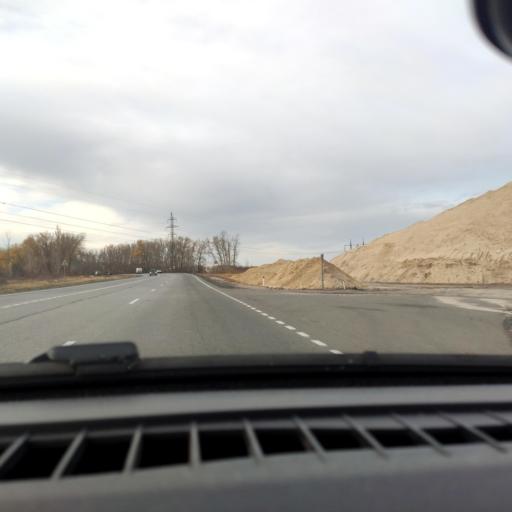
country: RU
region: Voronezj
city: Ostrogozhsk
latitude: 50.9441
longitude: 39.0549
